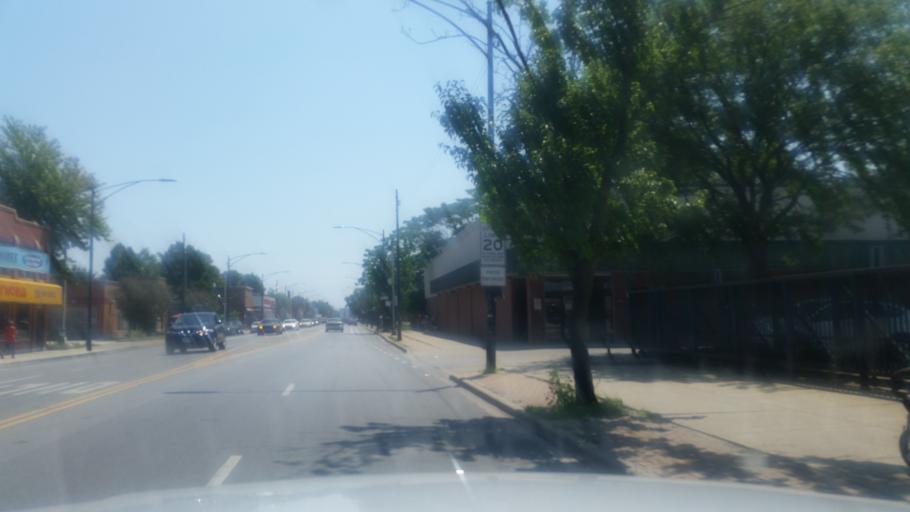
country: US
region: Illinois
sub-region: Cook County
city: Chicago
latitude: 41.7796
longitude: -87.6157
